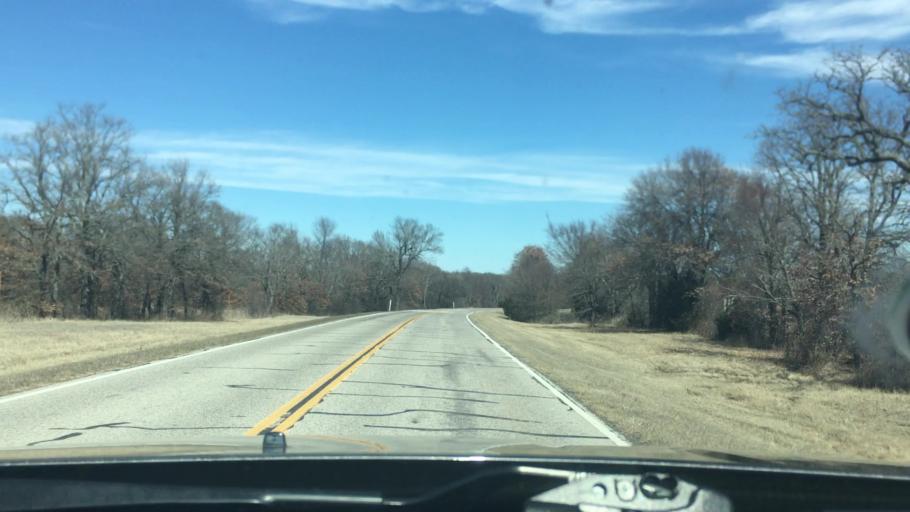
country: US
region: Oklahoma
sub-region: Carter County
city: Dickson
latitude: 34.3199
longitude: -96.9606
